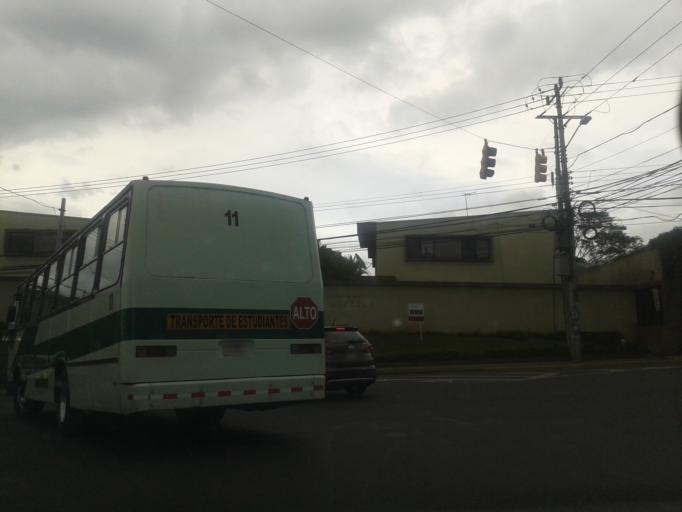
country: CR
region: San Jose
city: San Vicente de Moravia
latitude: 9.9631
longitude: -84.0549
